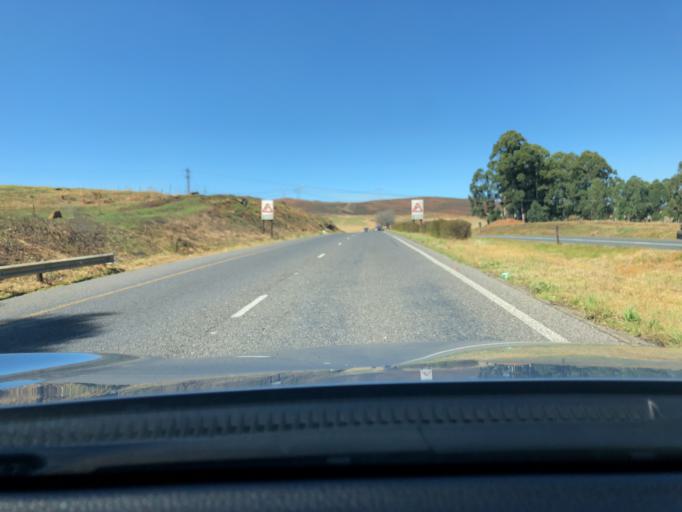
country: ZA
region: KwaZulu-Natal
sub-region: uMgungundlovu District Municipality
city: Howick
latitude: -29.4240
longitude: 30.1683
